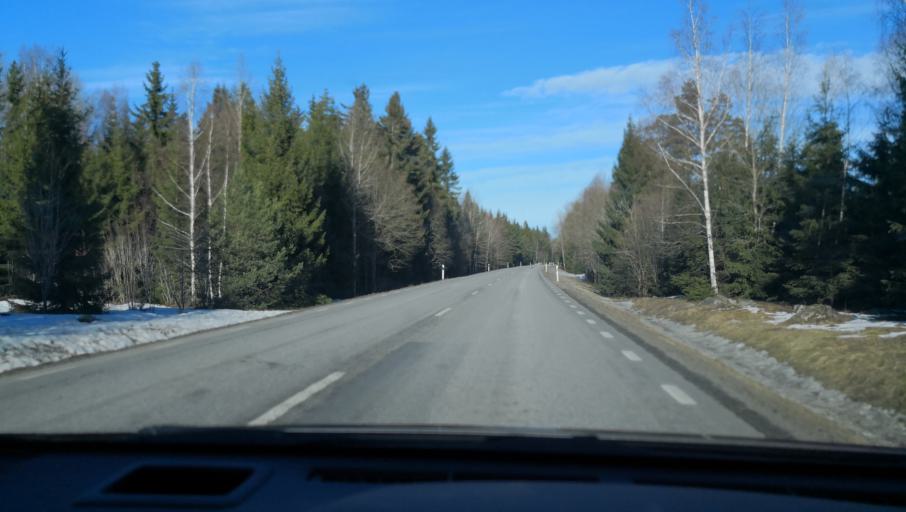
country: SE
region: Uppsala
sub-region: Uppsala Kommun
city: Vattholma
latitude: 60.0173
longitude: 17.7445
